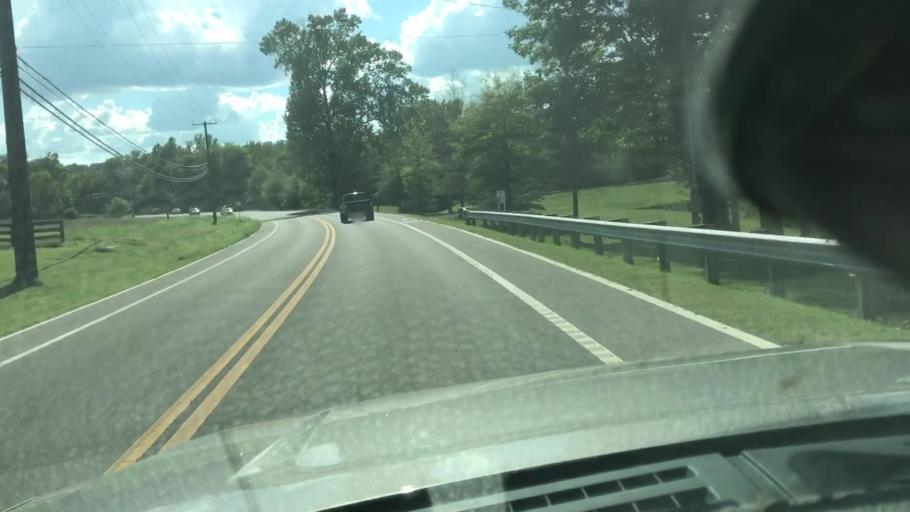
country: US
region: Tennessee
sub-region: Cheatham County
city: Pegram
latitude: 36.0265
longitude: -87.0213
